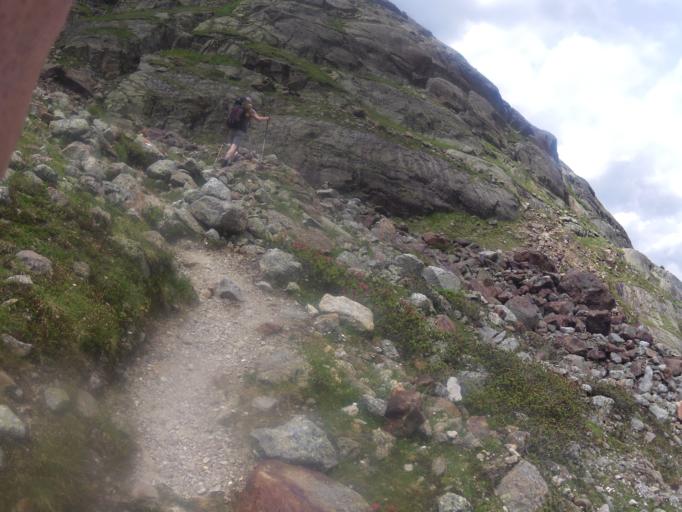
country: IT
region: Trentino-Alto Adige
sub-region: Bolzano
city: Racines
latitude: 46.9888
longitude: 11.2240
